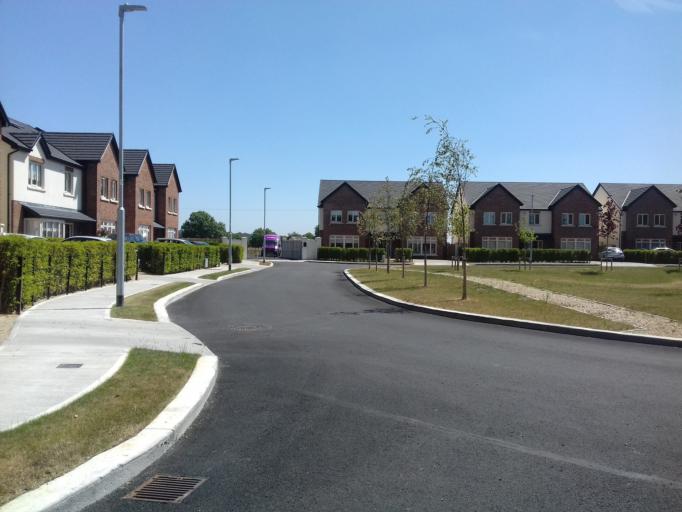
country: IE
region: Leinster
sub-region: Fingal County
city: Swords
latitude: 53.5177
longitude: -6.2655
